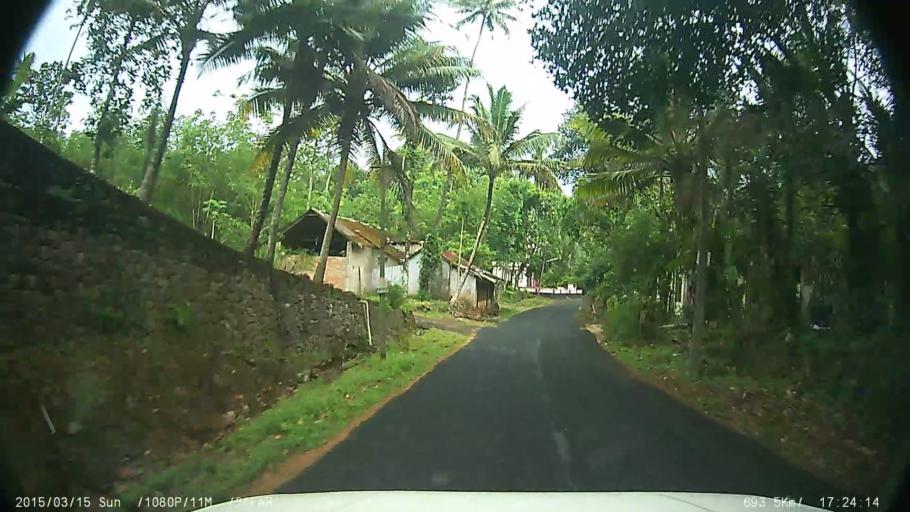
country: IN
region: Kerala
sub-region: Kottayam
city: Lalam
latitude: 9.8304
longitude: 76.7171
